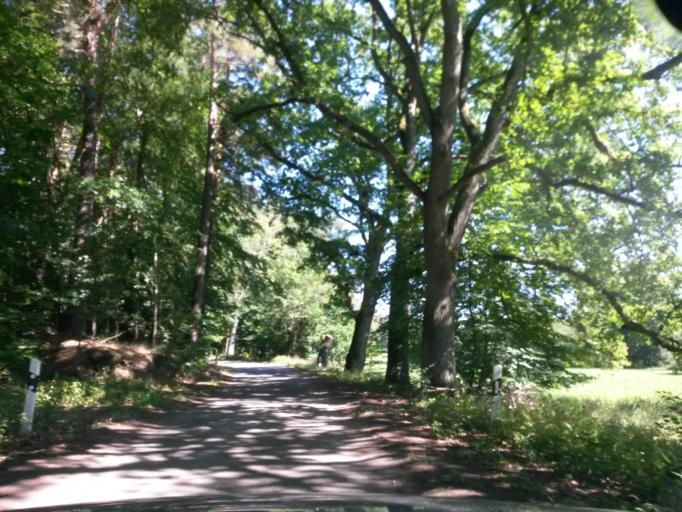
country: DE
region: Brandenburg
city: Templin
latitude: 53.2325
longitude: 13.4559
